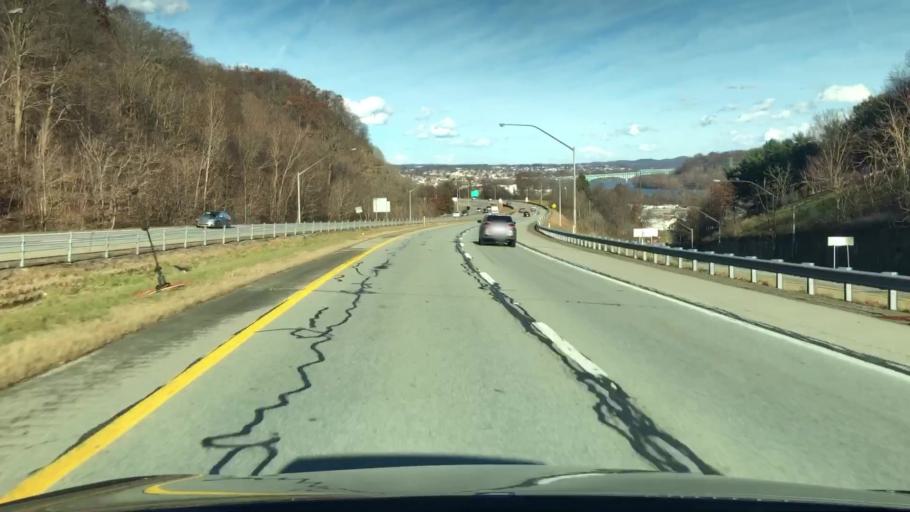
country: US
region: Pennsylvania
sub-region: Westmoreland County
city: Arnold
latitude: 40.5800
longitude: -79.7840
